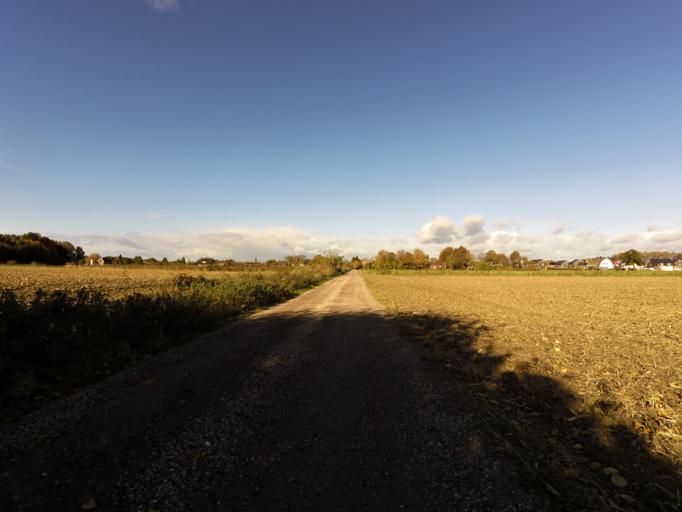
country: NL
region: Gelderland
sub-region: Gemeente Doetinchem
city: Doetinchem
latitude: 51.9494
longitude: 6.2125
